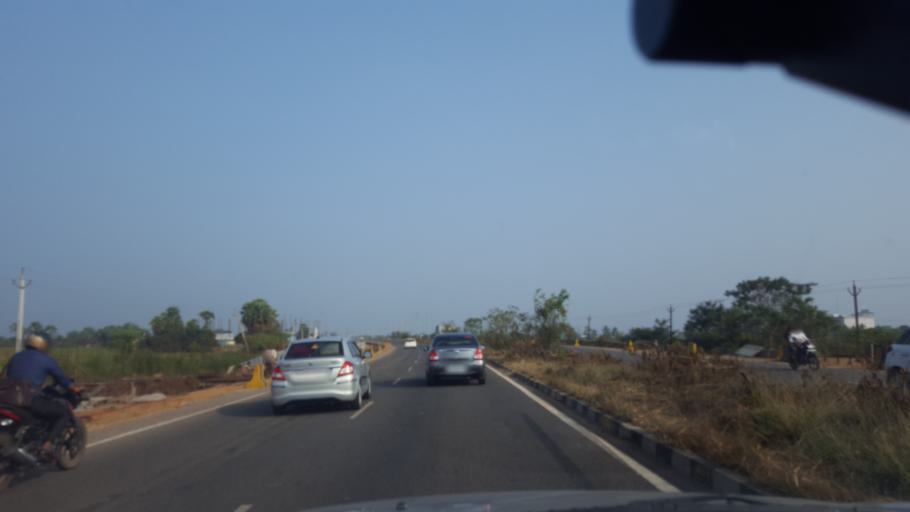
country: IN
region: Andhra Pradesh
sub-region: West Godavari
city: Eluru
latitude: 16.7400
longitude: 81.0983
